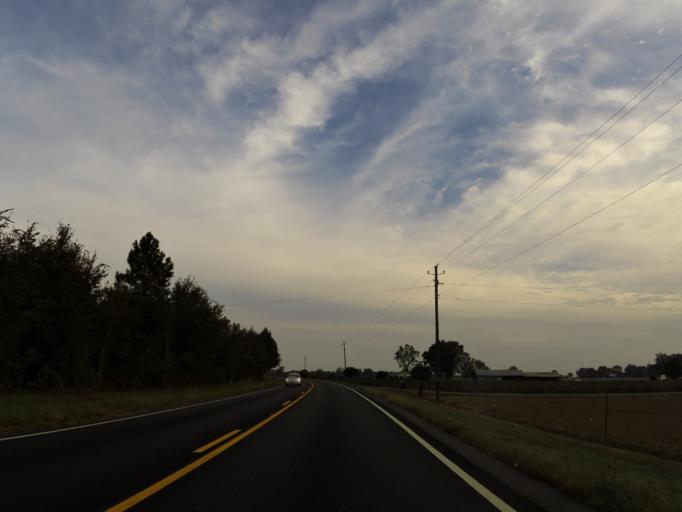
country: US
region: Alabama
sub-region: Escambia County
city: Atmore
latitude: 31.2294
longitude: -87.4796
